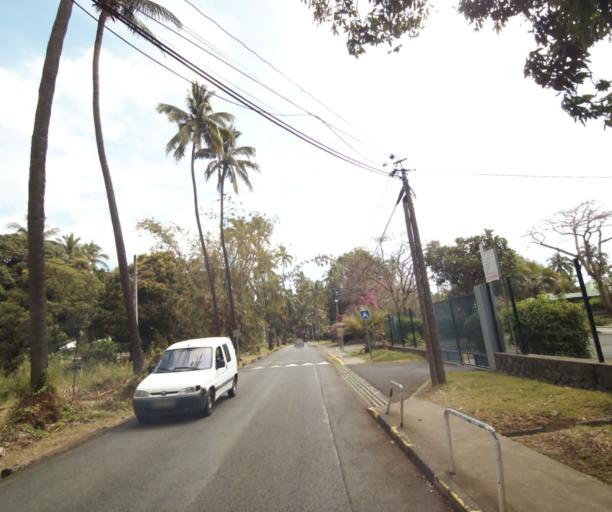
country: RE
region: Reunion
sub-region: Reunion
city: Saint-Paul
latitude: -21.0105
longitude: 55.2835
